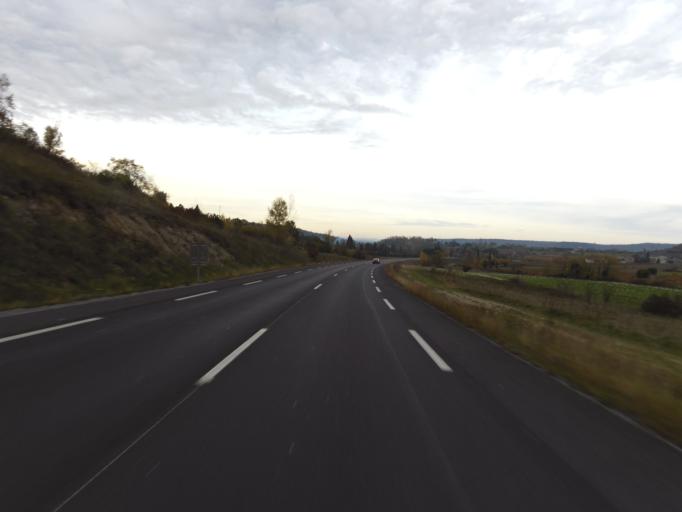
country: FR
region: Rhone-Alpes
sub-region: Departement de l'Ardeche
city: Joyeuse
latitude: 44.4746
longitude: 4.2397
